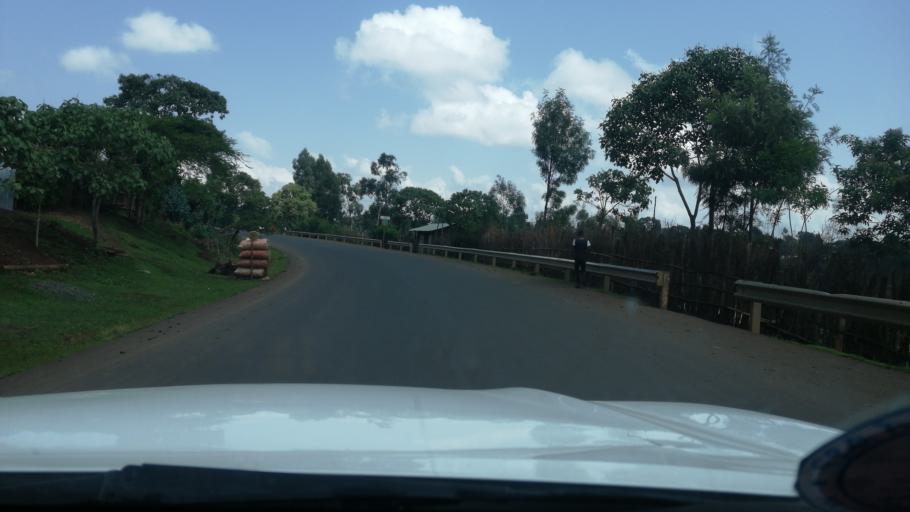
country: ET
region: Oromiya
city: Gedo
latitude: 8.9819
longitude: 37.5972
